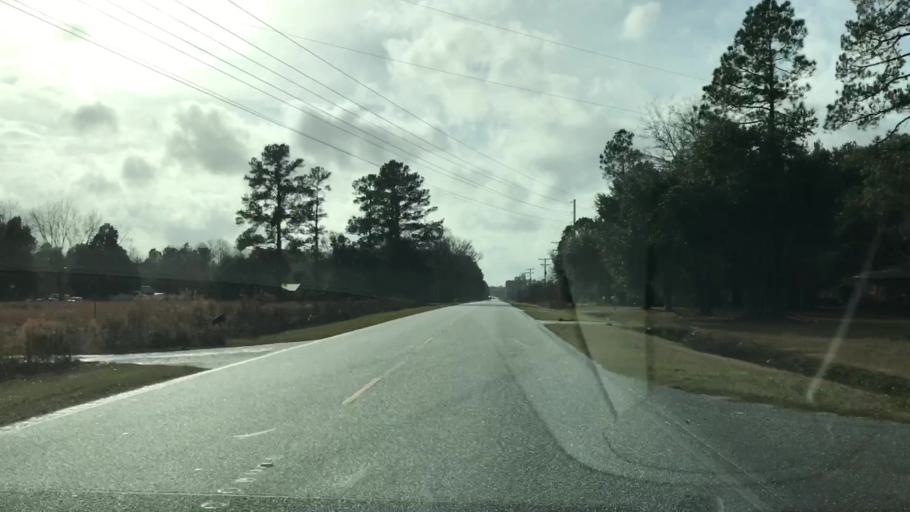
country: US
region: South Carolina
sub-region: Williamsburg County
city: Andrews
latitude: 33.5016
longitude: -79.5284
